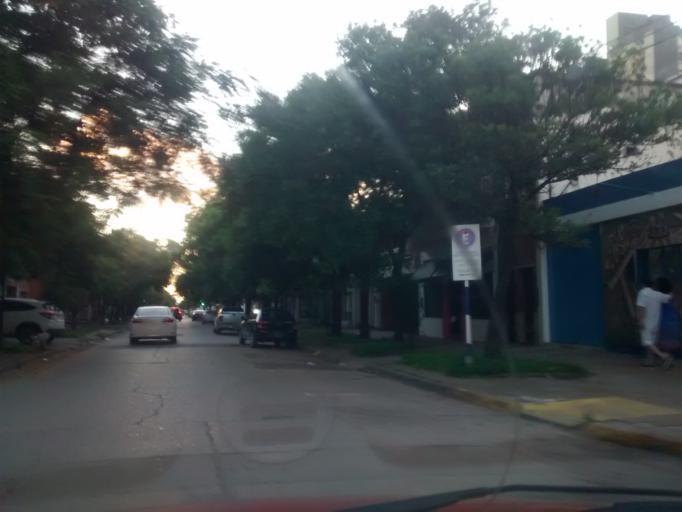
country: AR
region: Chaco
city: Resistencia
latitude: -27.4504
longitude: -58.9821
